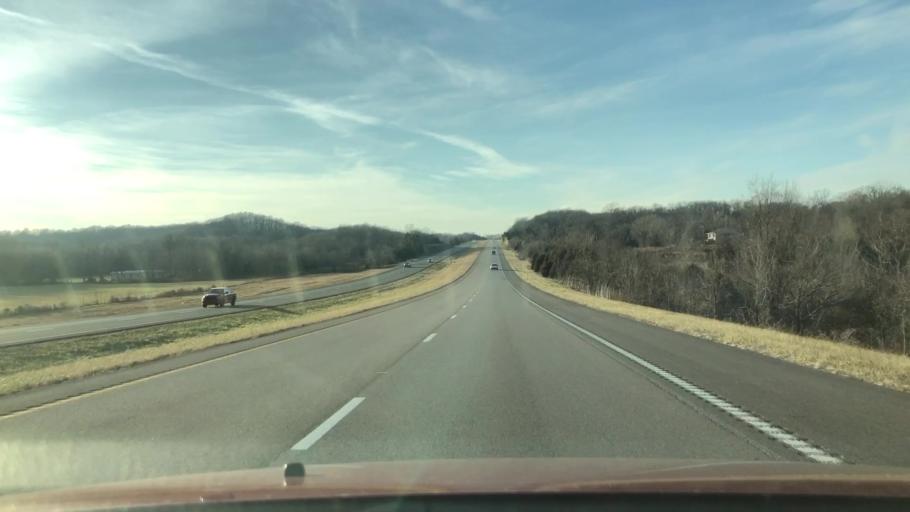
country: US
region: Missouri
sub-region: Wright County
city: Mansfield
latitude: 37.1115
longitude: -92.6529
